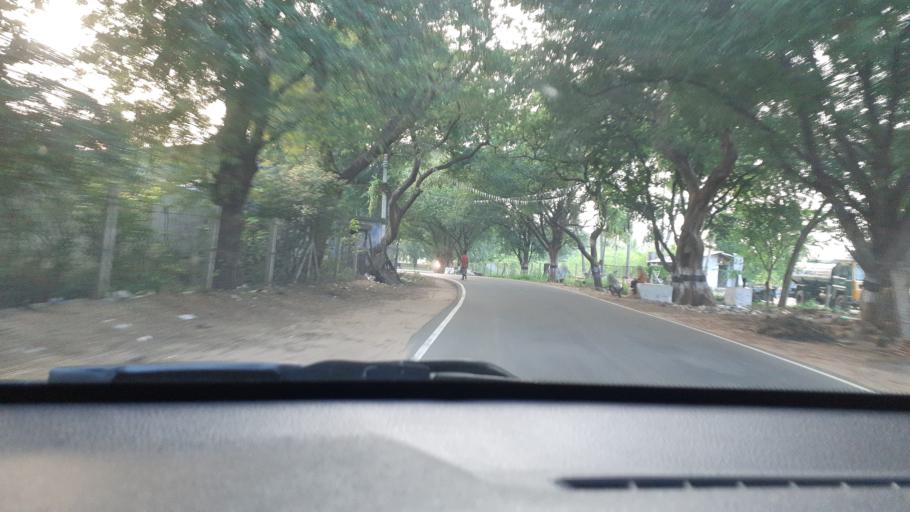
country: IN
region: Tamil Nadu
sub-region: Dindigul
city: Palani
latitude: 10.4293
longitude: 77.5277
